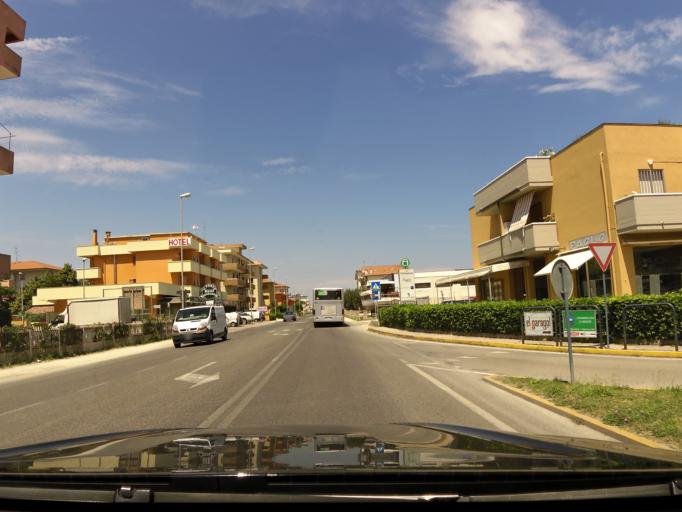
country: IT
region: The Marches
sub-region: Provincia di Pesaro e Urbino
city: Marotta
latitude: 43.7639
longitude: 13.1463
